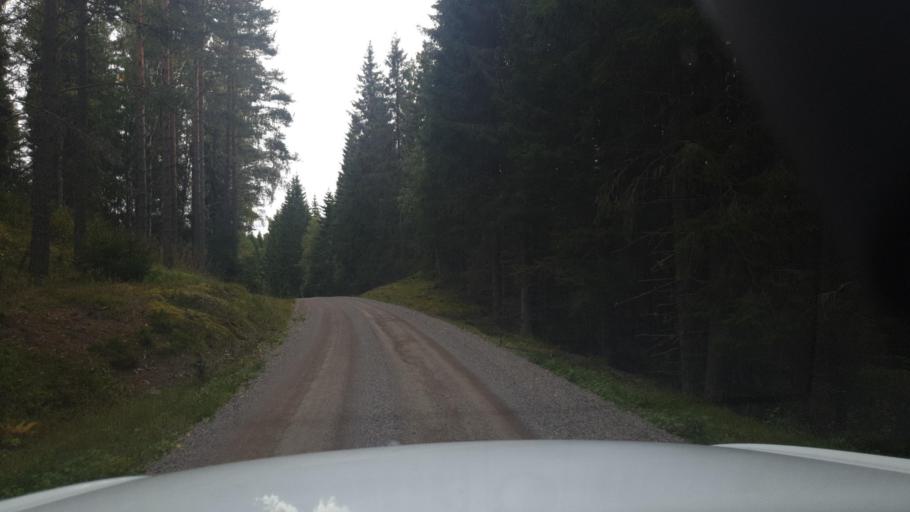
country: SE
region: Vaermland
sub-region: Eda Kommun
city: Charlottenberg
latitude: 60.0316
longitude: 12.6320
